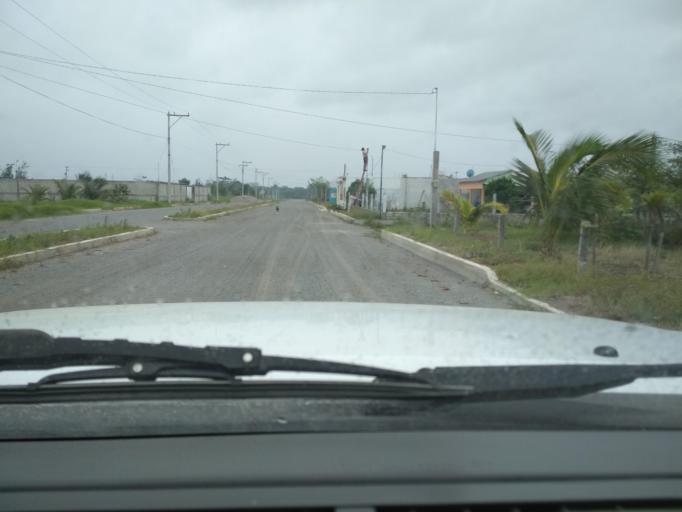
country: MX
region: Veracruz
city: Paso del Toro
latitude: 19.0430
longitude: -96.1340
